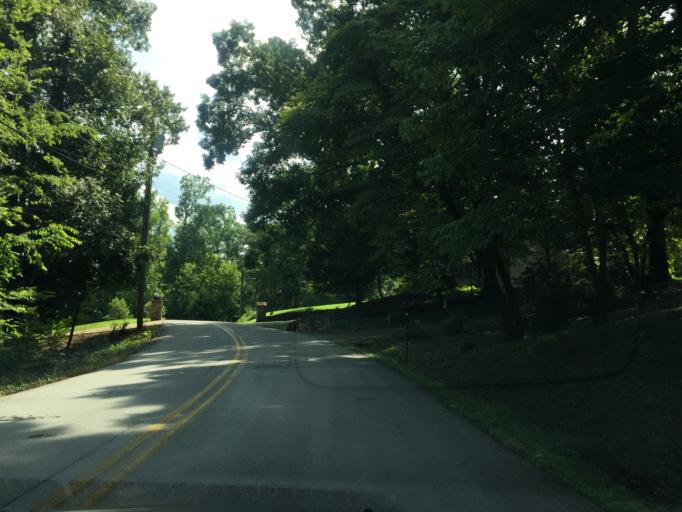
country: US
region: Tennessee
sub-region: Hamilton County
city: East Chattanooga
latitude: 35.0981
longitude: -85.1980
